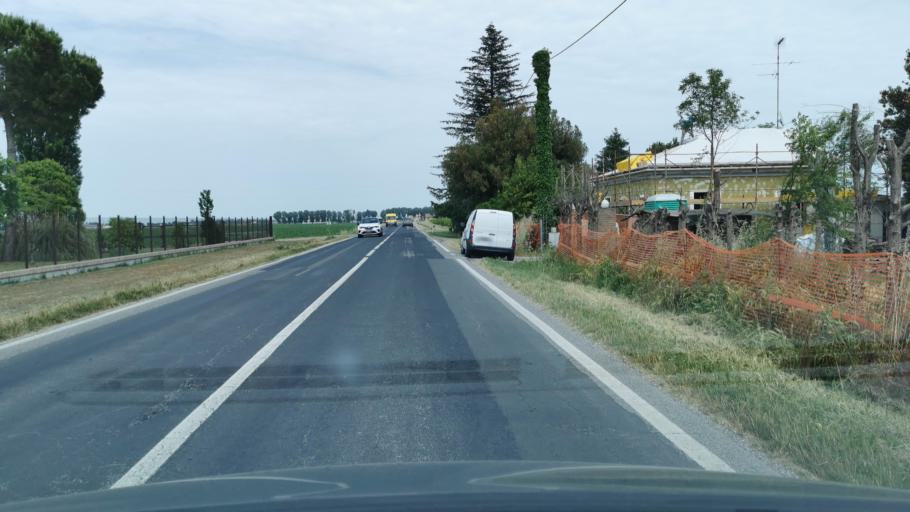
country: IT
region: Emilia-Romagna
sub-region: Provincia di Ravenna
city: Glorie
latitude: 44.4940
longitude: 12.0771
